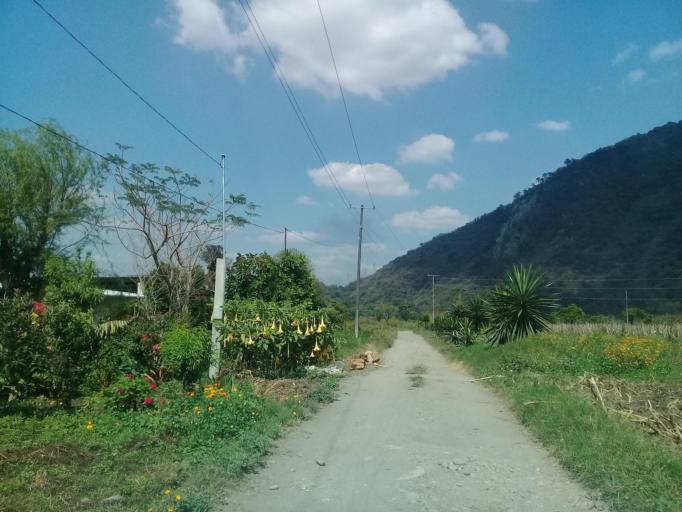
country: MX
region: Veracruz
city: Jalapilla
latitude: 18.8283
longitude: -97.0743
